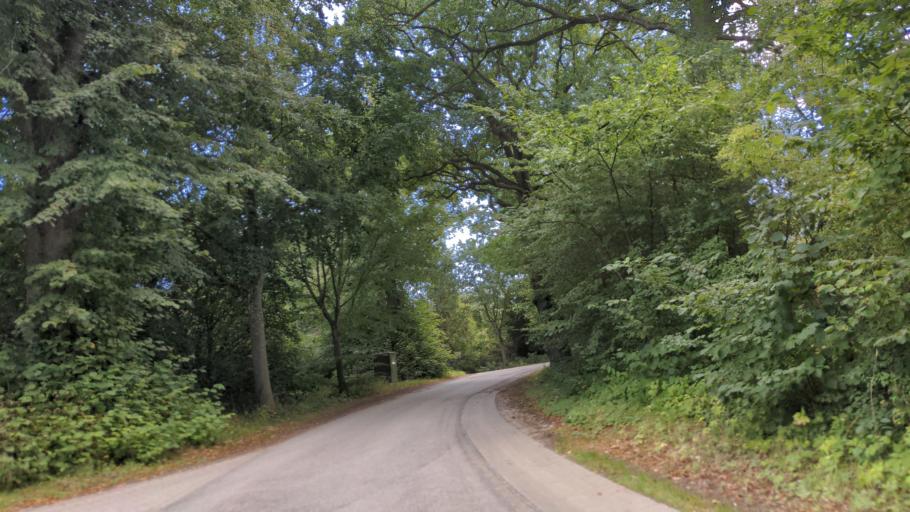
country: DE
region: Schleswig-Holstein
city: Kasseedorf
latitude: 54.1593
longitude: 10.6904
